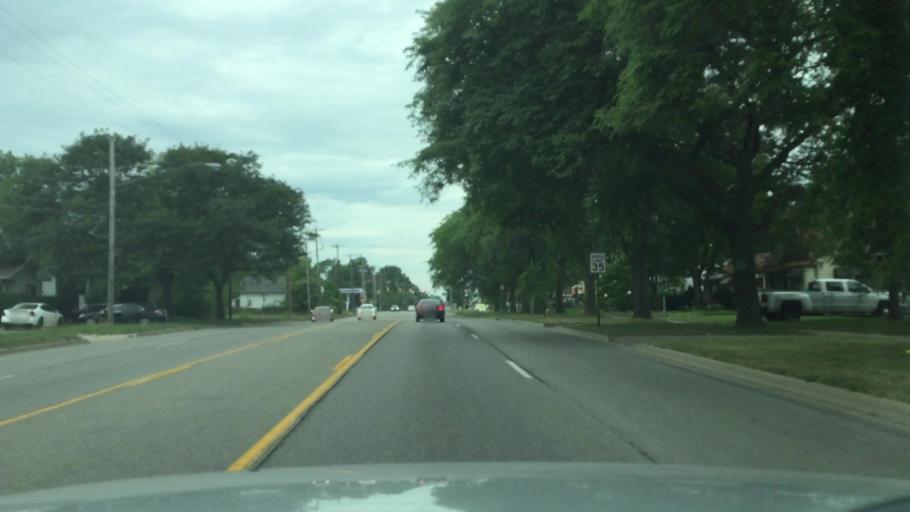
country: US
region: Michigan
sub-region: Genesee County
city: Beecher
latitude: 43.0609
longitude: -83.7203
